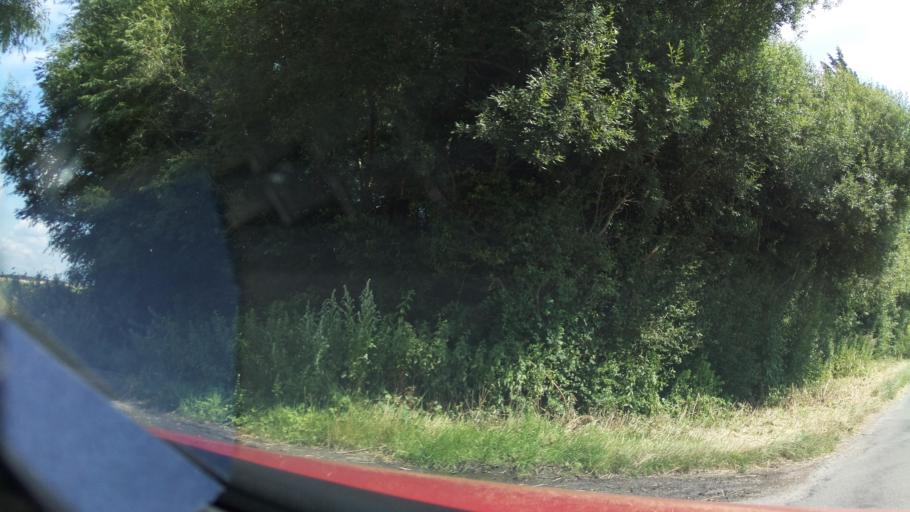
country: GB
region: England
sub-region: Borough of Swindon
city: Bishopstone
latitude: 51.5696
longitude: -1.6278
